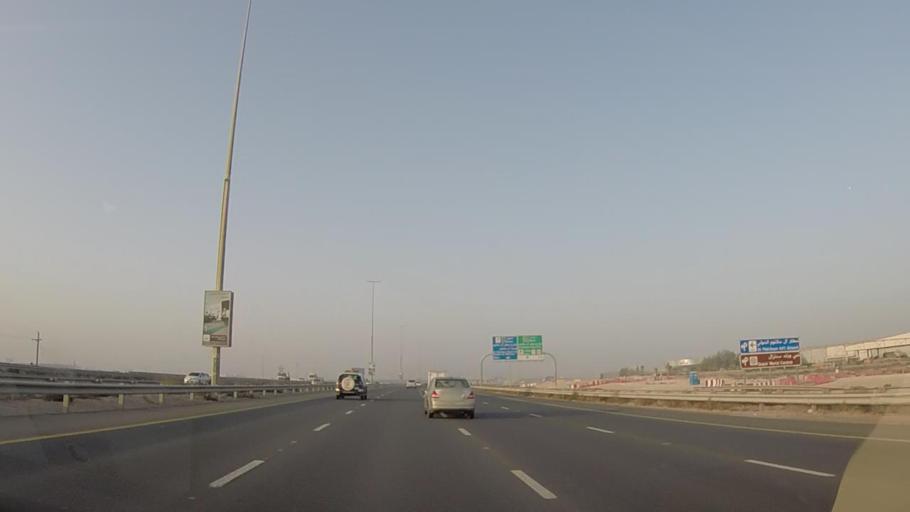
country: AE
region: Dubai
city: Dubai
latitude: 24.9506
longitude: 55.0706
